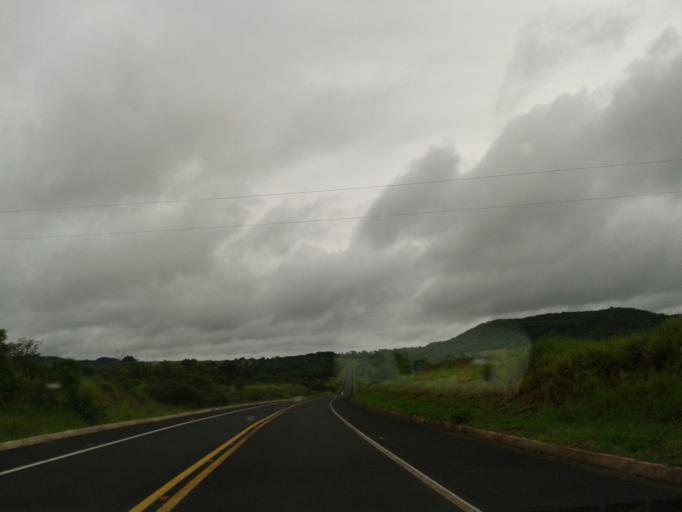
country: BR
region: Minas Gerais
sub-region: Santa Vitoria
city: Santa Vitoria
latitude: -19.2247
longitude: -50.0200
